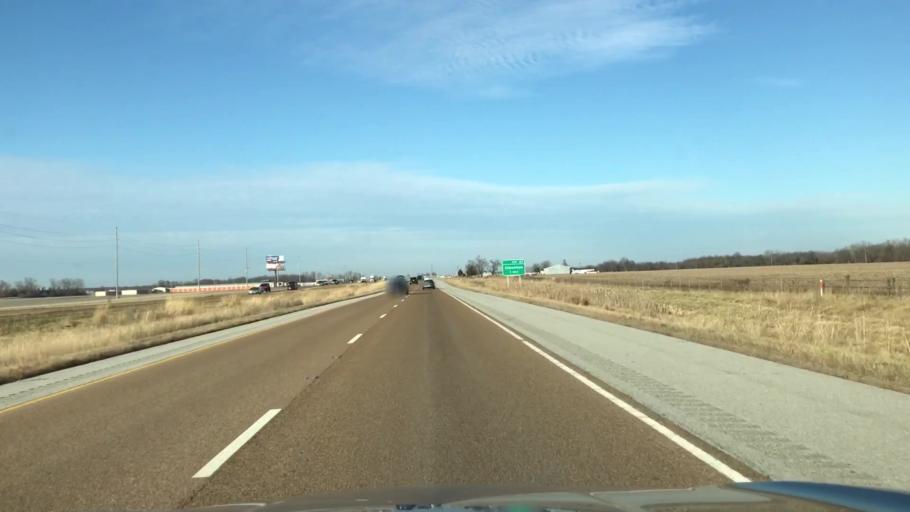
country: US
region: Illinois
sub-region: Macoupin County
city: Staunton
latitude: 38.9998
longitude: -89.7496
